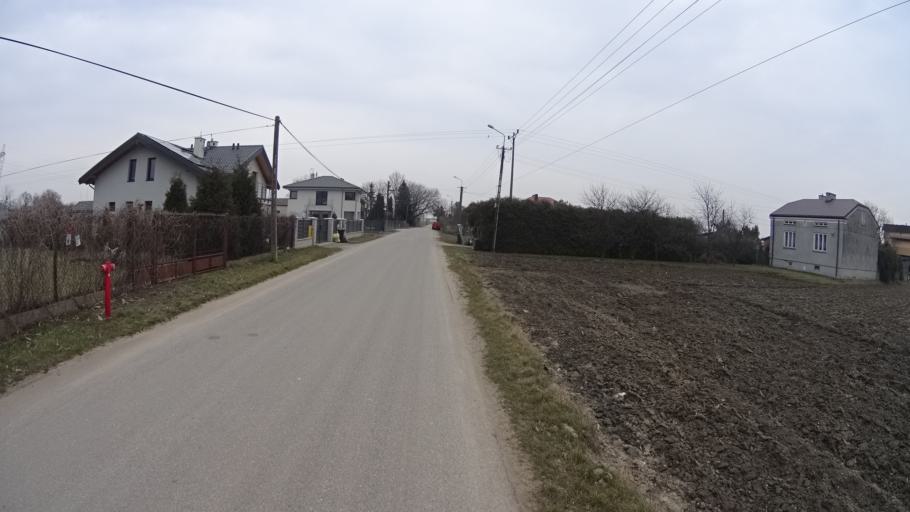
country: PL
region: Masovian Voivodeship
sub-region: Powiat warszawski zachodni
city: Ozarow Mazowiecki
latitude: 52.2241
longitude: 20.8212
